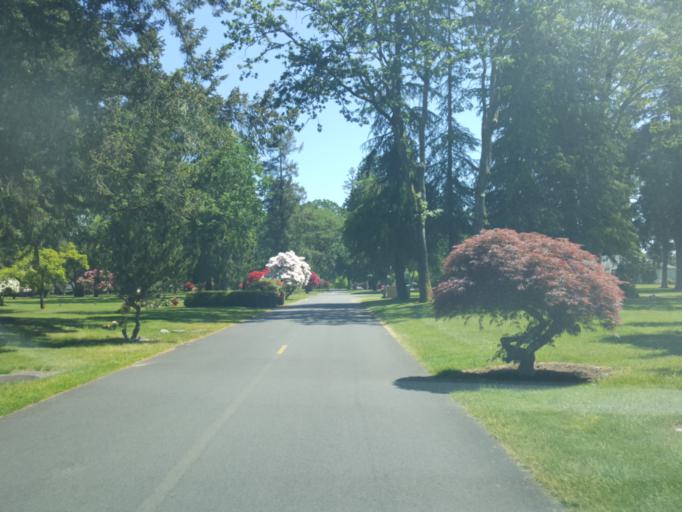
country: US
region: Washington
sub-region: Pierce County
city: University Place
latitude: 47.2000
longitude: -122.5617
